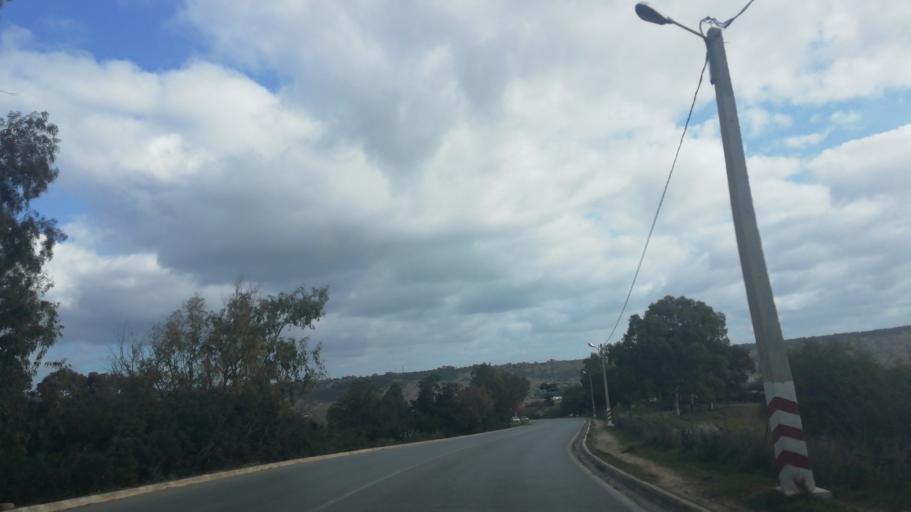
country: DZ
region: Relizane
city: Mazouna
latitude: 36.2950
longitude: 0.6565
